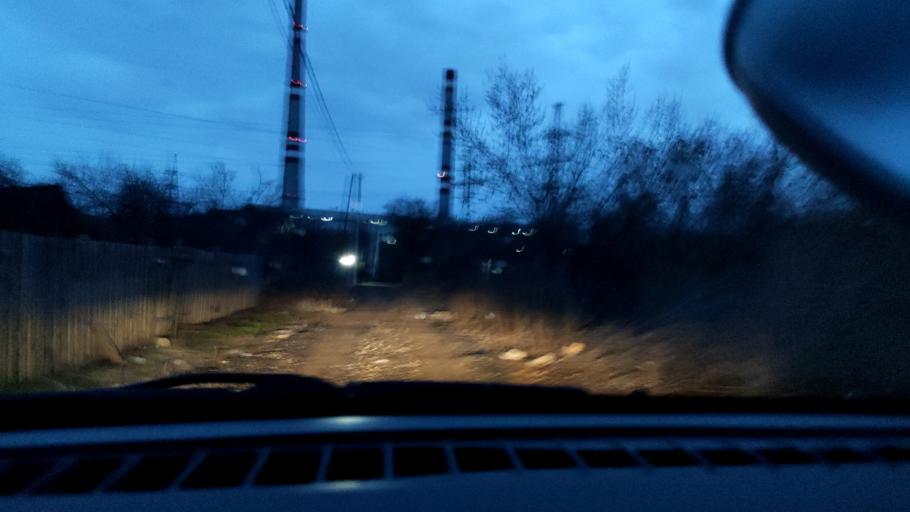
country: RU
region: Samara
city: Petra-Dubrava
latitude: 53.2559
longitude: 50.2744
